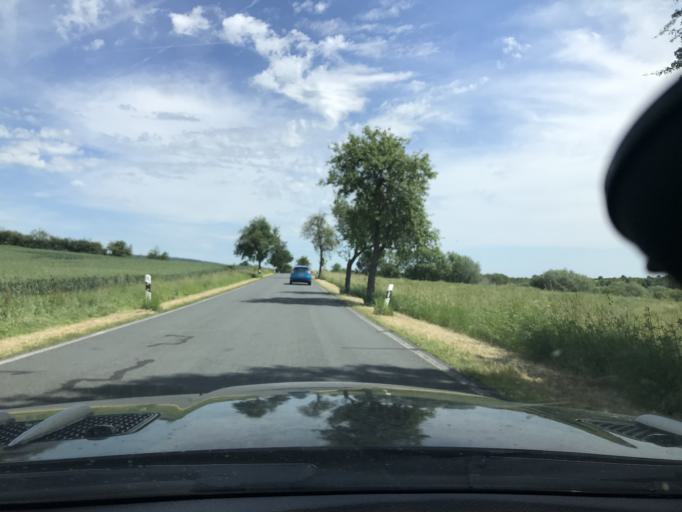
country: DE
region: Thuringia
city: Muehlhausen
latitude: 51.2536
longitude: 10.4323
